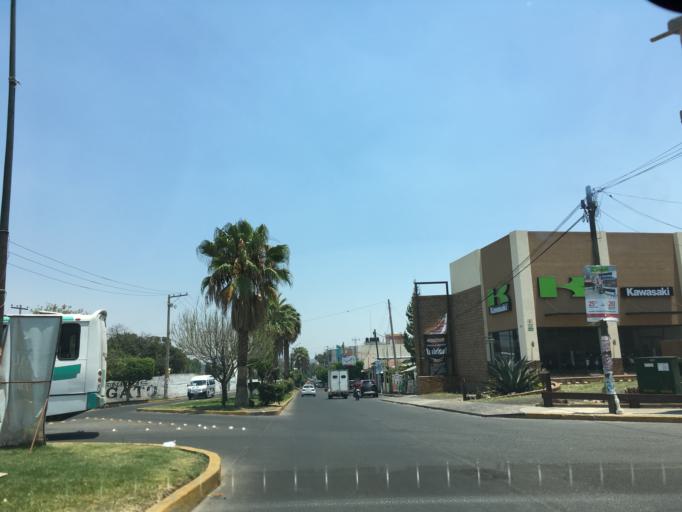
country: MX
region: Guanajuato
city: Uriangato
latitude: 20.1288
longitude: -101.1799
